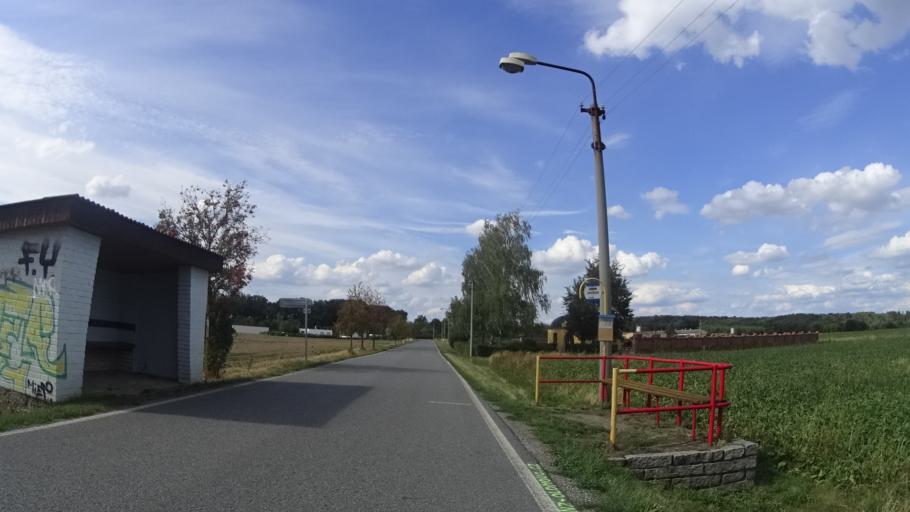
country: CZ
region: Olomoucky
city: Moravicany
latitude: 49.7410
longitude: 16.9740
